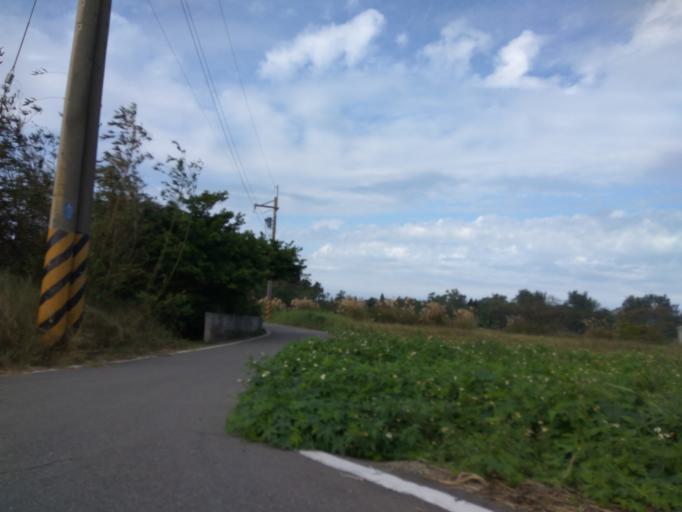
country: TW
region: Taiwan
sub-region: Hsinchu
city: Zhubei
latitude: 24.9582
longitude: 121.0062
